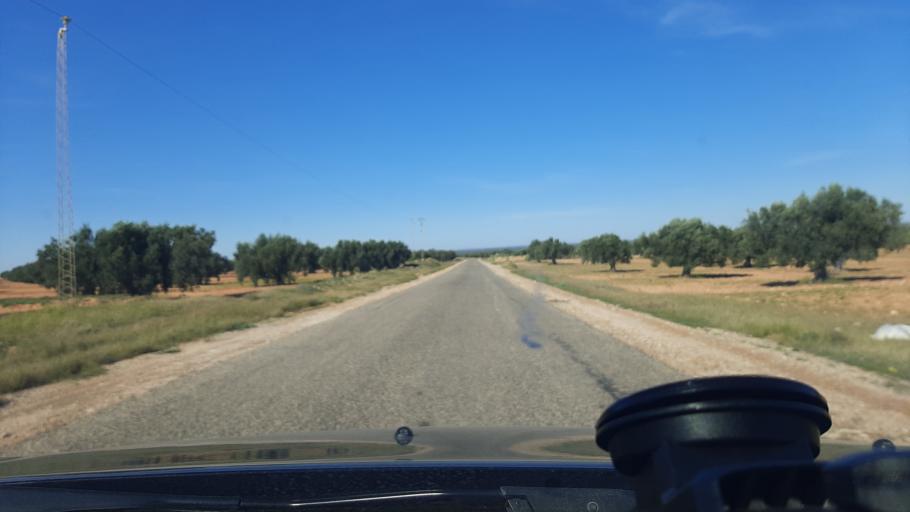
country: TN
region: Safaqis
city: Sfax
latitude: 34.9624
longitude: 10.5406
